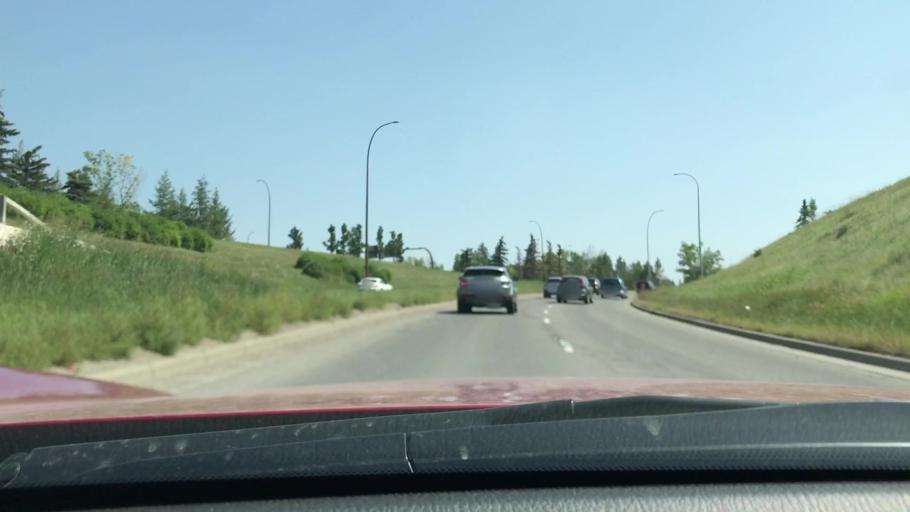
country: CA
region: Alberta
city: Calgary
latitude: 50.9939
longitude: -114.0966
